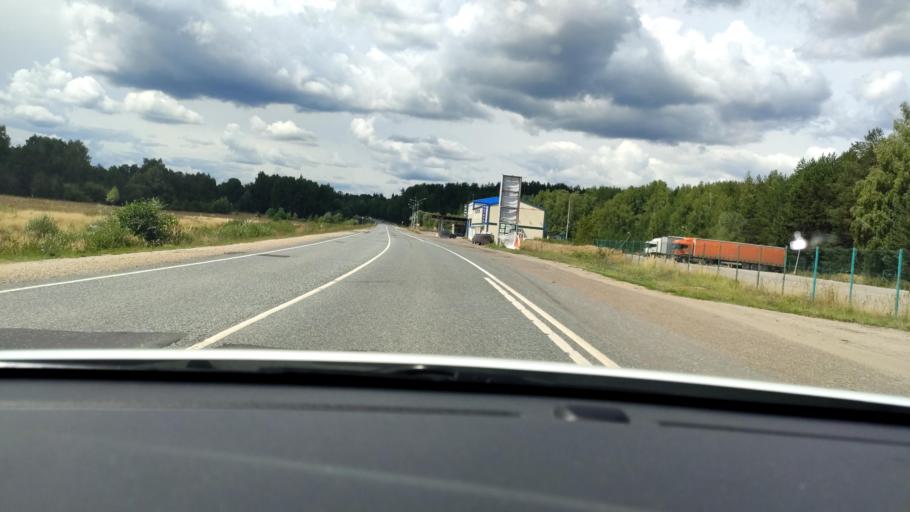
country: RU
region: Tatarstan
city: Aysha
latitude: 55.8801
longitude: 48.6534
